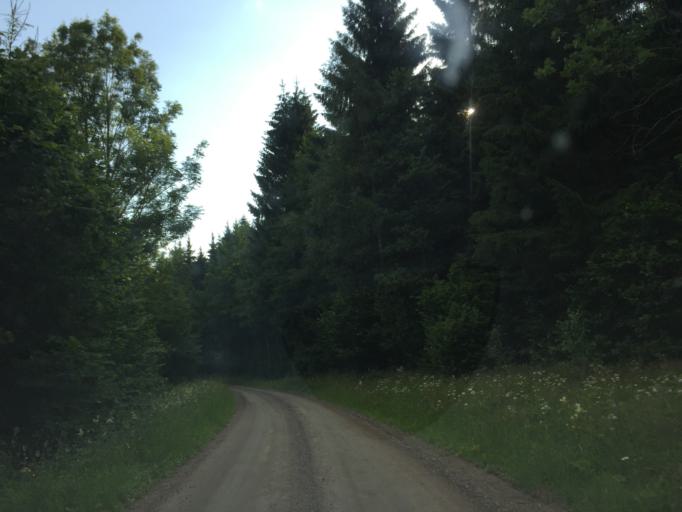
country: SE
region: OEstergoetland
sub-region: Motala Kommun
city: Ryd
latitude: 58.7012
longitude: 15.0176
